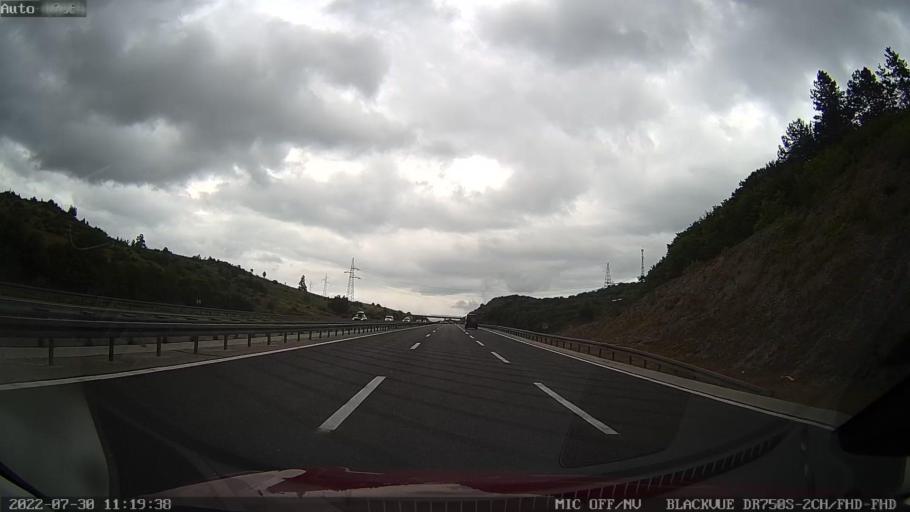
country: HR
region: Licko-Senjska
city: Brinje
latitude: 45.0127
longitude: 15.1390
